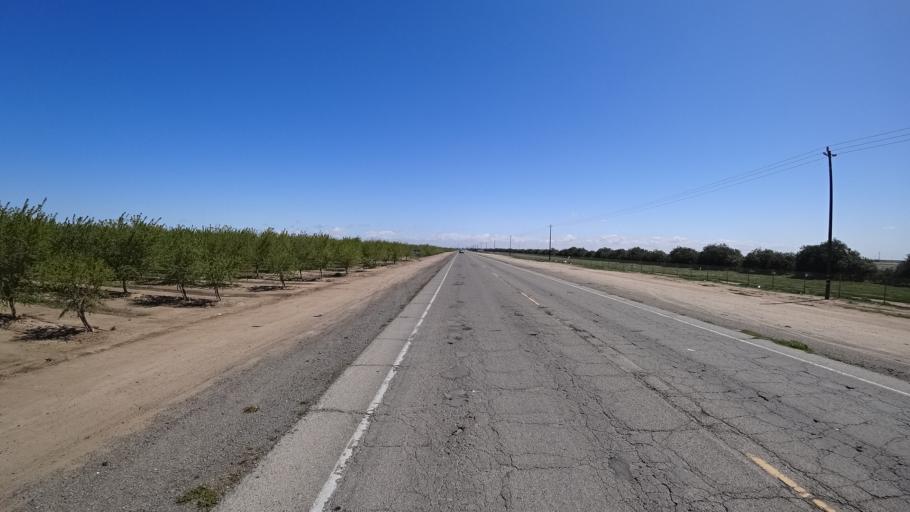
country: US
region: California
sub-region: Fresno County
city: West Park
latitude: 36.7063
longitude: -119.9242
